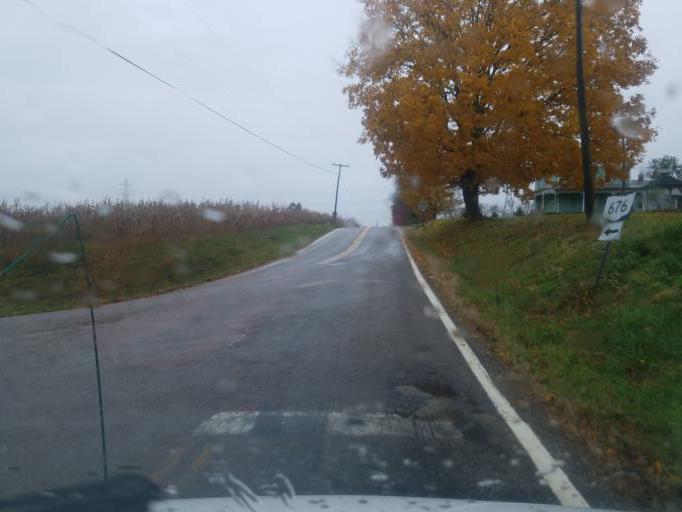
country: US
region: Ohio
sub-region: Washington County
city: Beverly
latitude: 39.4717
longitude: -81.7138
